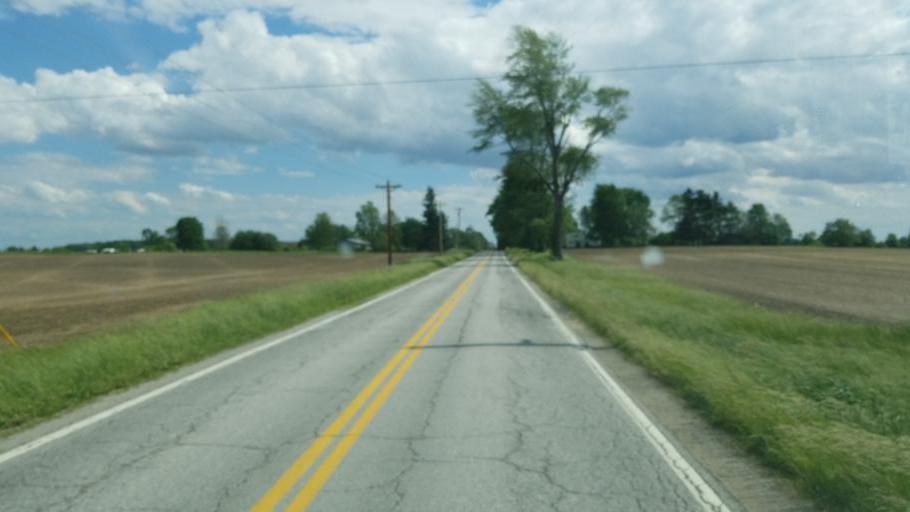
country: US
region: Ohio
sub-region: Huron County
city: Plymouth
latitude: 41.0359
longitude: -82.6081
